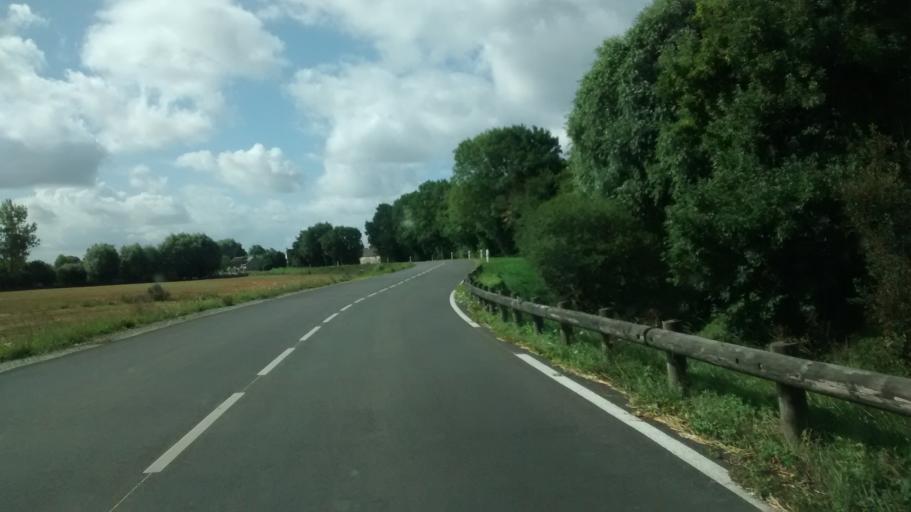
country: FR
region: Brittany
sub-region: Departement d'Ille-et-Vilaine
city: Le Vivier-sur-Mer
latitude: 48.5829
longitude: -1.7804
